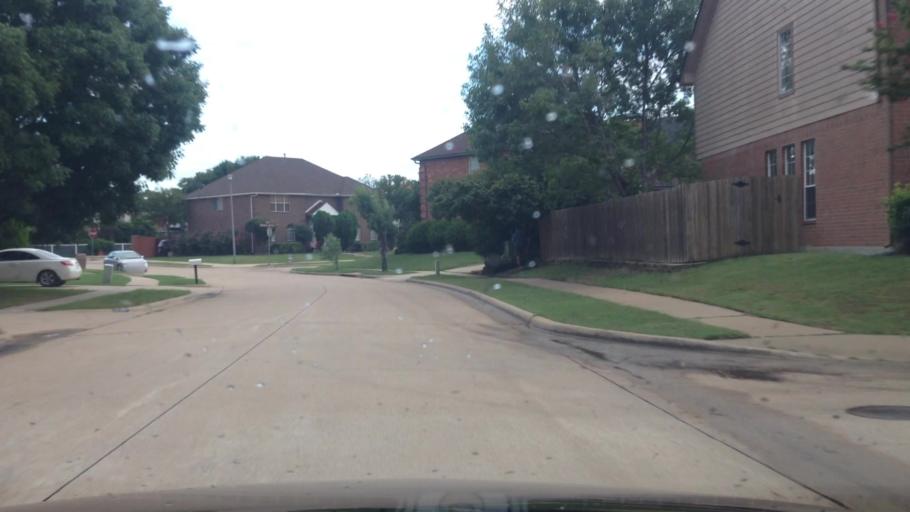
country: US
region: Texas
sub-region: Denton County
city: Flower Mound
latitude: 33.0182
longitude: -97.0627
